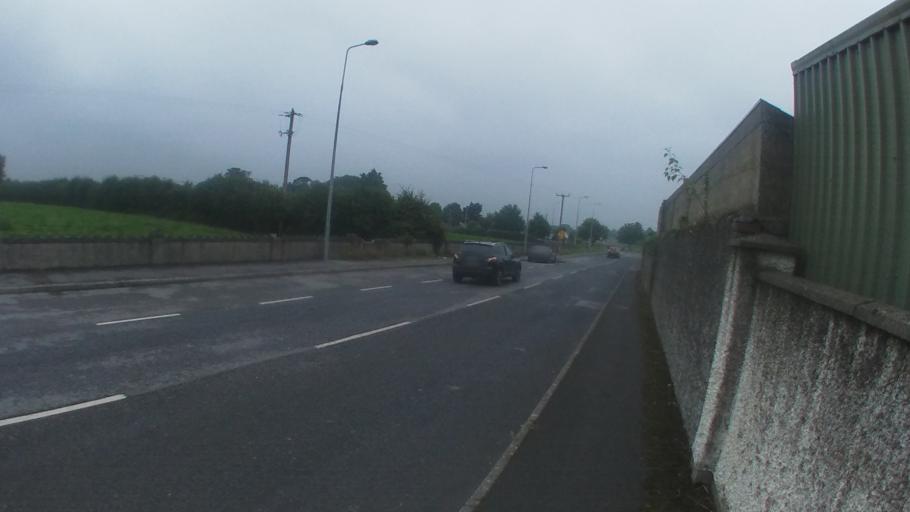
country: IE
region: Leinster
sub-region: Kilkenny
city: Callan
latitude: 52.5493
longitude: -7.3896
